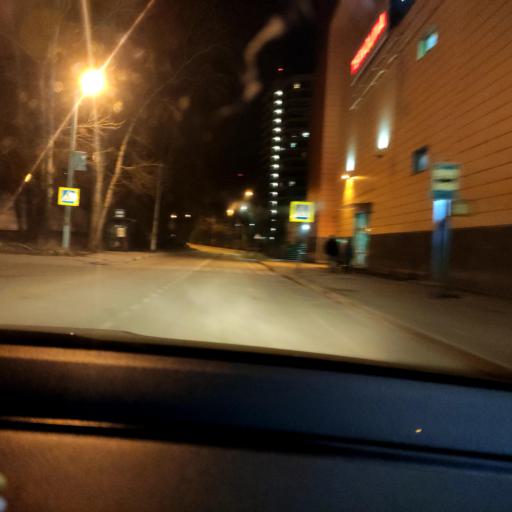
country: RU
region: Moskovskaya
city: Krasnogorsk
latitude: 55.8297
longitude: 37.3076
